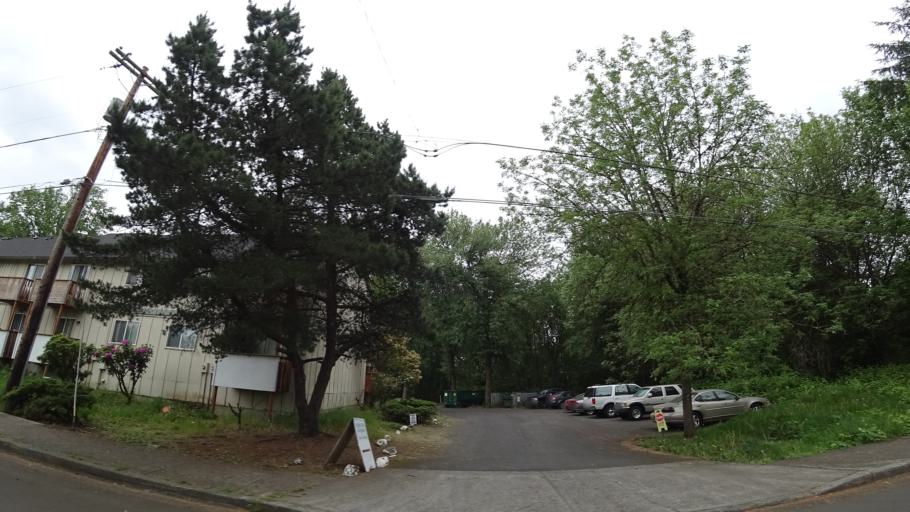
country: US
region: Oregon
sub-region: Washington County
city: Beaverton
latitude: 45.4892
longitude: -122.7846
